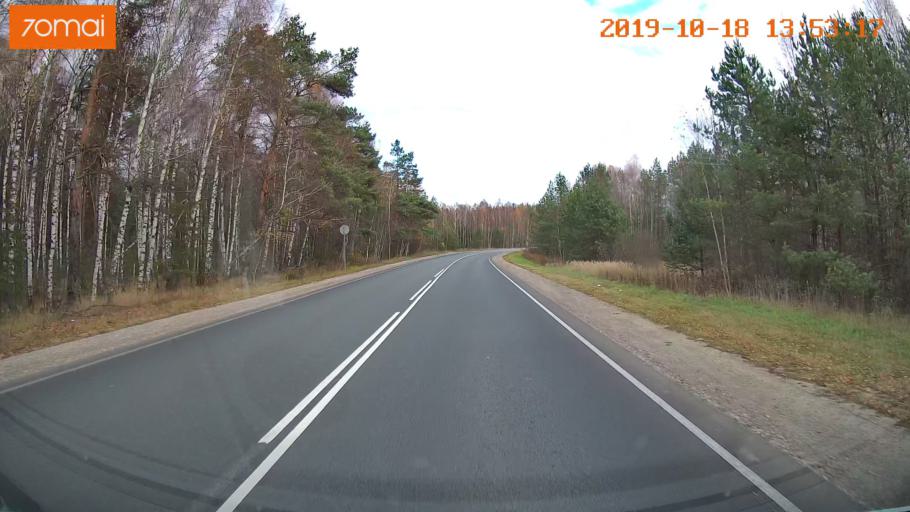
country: RU
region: Moskovskaya
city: Radovitskiy
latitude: 55.0374
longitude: 39.9784
